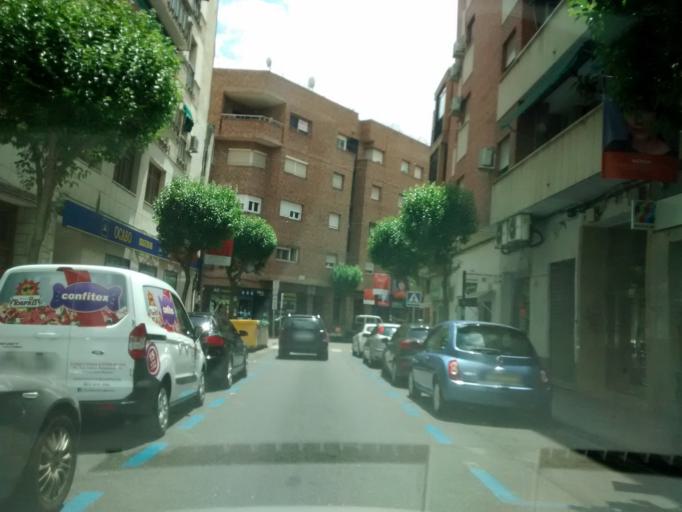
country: ES
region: Extremadura
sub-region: Provincia de Badajoz
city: Merida
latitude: 38.9186
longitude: -6.3438
